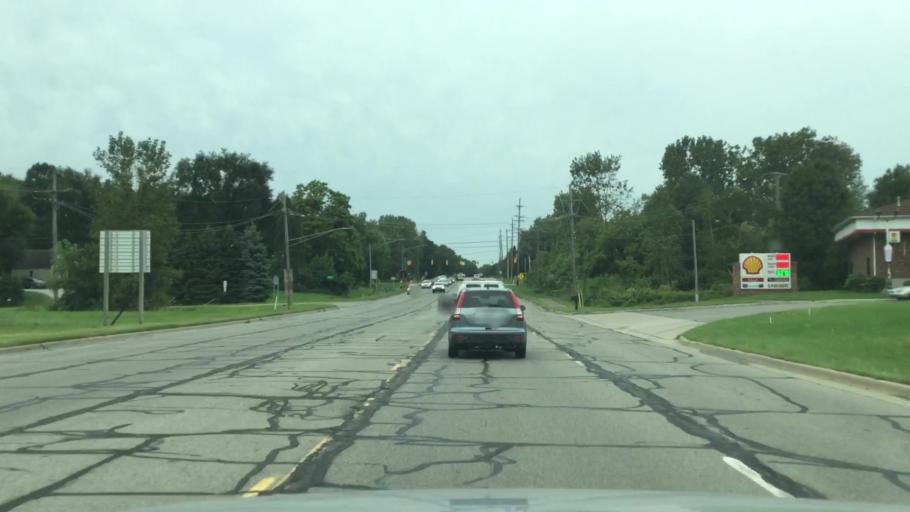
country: US
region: Michigan
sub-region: Washtenaw County
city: Ypsilanti
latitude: 42.2209
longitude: -83.6579
